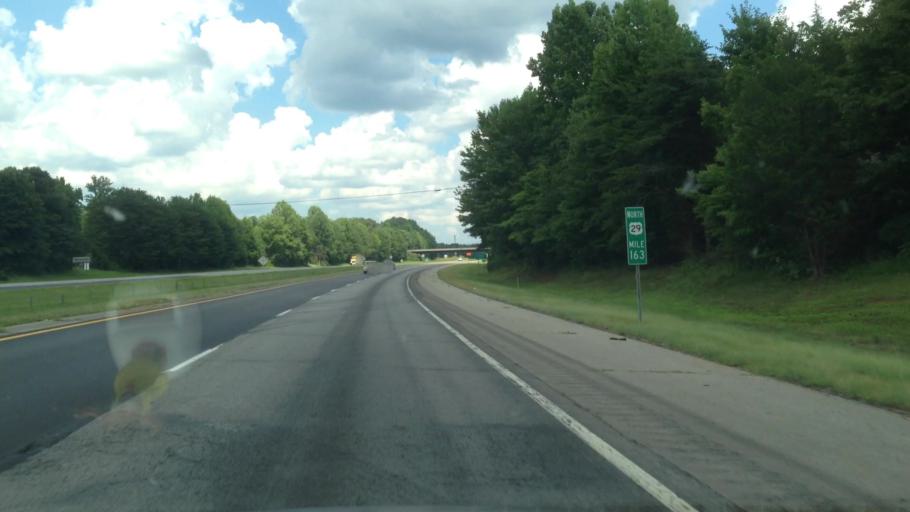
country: US
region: Virginia
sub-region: City of Danville
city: Danville
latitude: 36.4717
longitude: -79.5205
